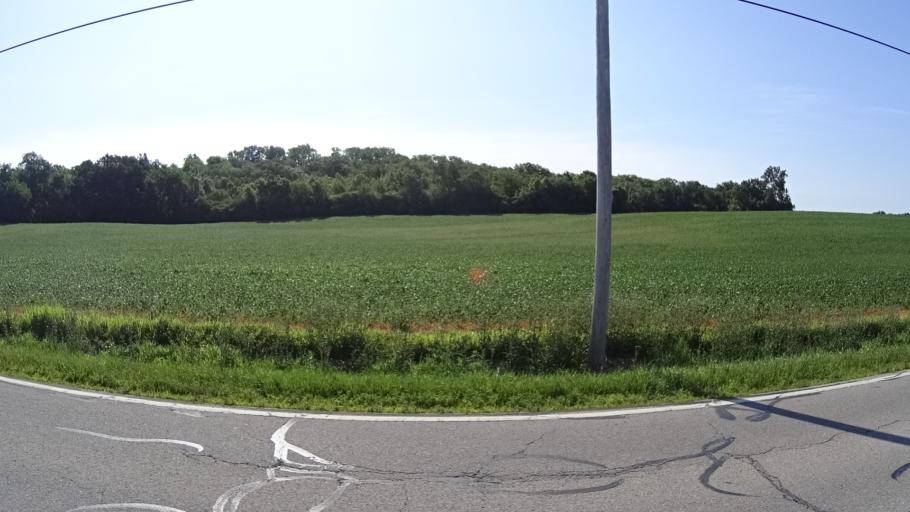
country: US
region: Ohio
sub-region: Huron County
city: Bellevue
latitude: 41.3812
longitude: -82.8382
